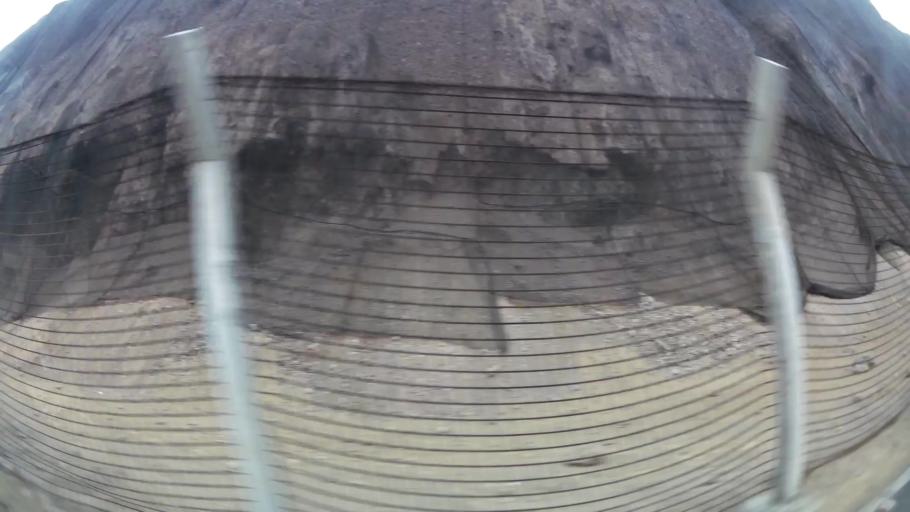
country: PE
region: Lima
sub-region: Lima
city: San Isidro
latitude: -12.1241
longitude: -77.0406
